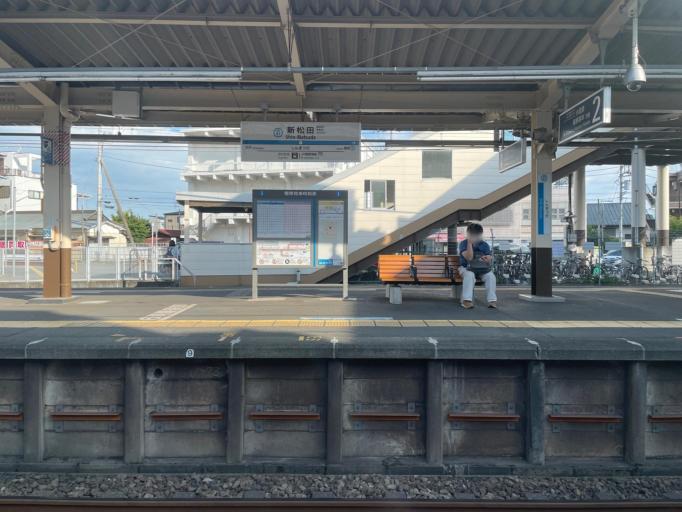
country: JP
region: Kanagawa
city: Hadano
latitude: 35.3448
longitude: 139.1399
